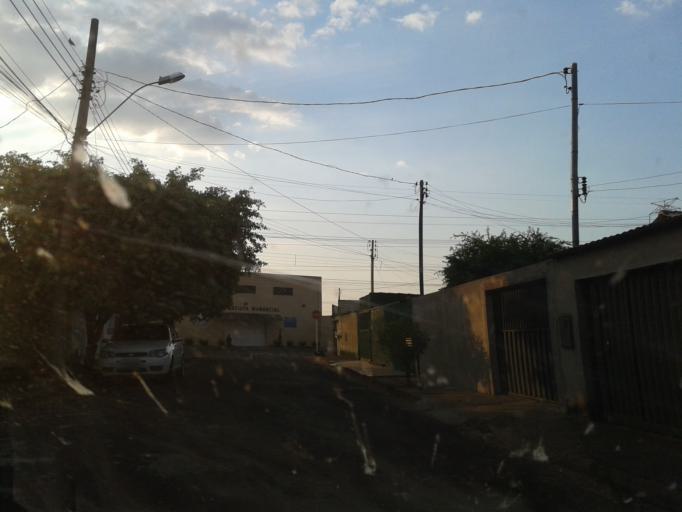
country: BR
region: Minas Gerais
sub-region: Uberlandia
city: Uberlandia
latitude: -18.9143
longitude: -48.3360
